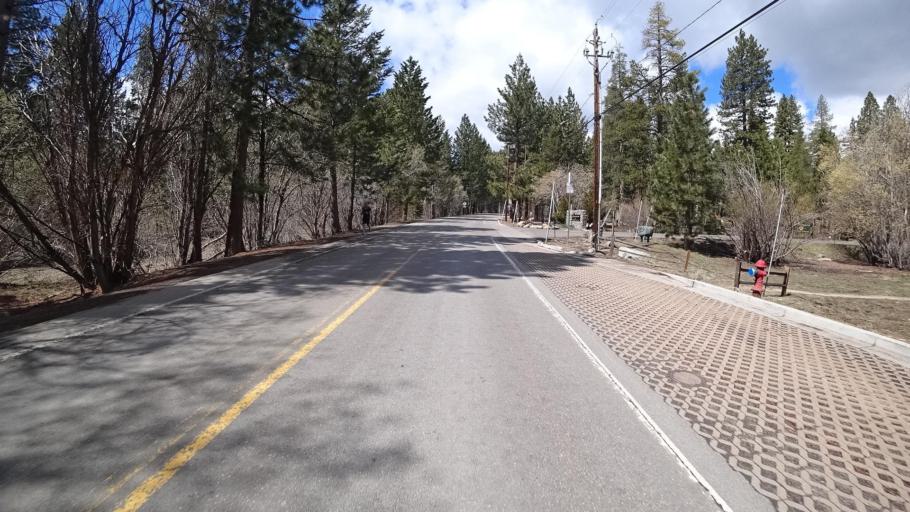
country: US
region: Nevada
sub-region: Washoe County
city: Incline Village
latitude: 39.2429
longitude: -119.9434
